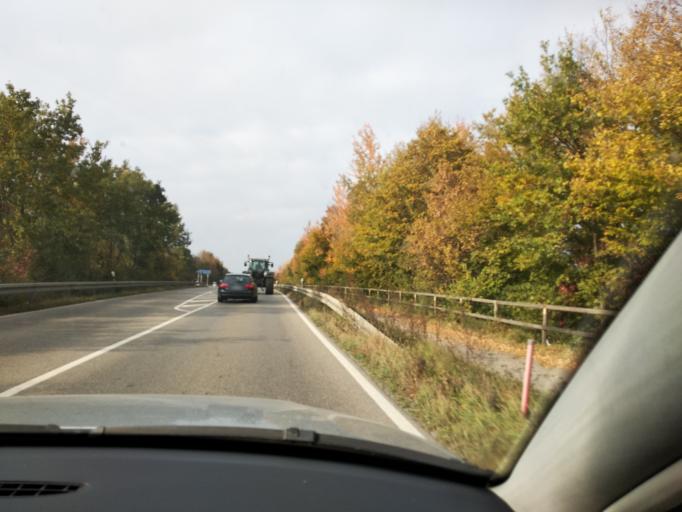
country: DE
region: Bavaria
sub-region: Upper Bavaria
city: Forstinning
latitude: 48.1682
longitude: 11.8923
